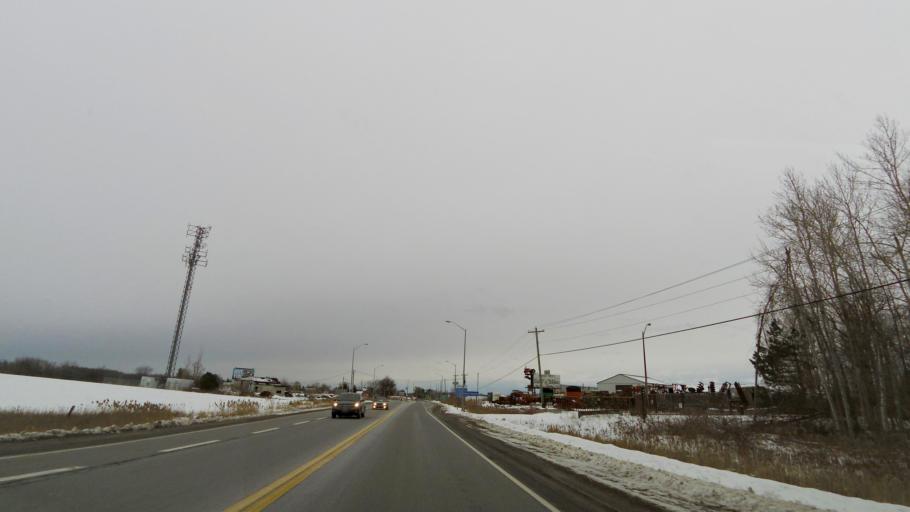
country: CA
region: Ontario
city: Ancaster
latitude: 43.2830
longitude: -80.0731
